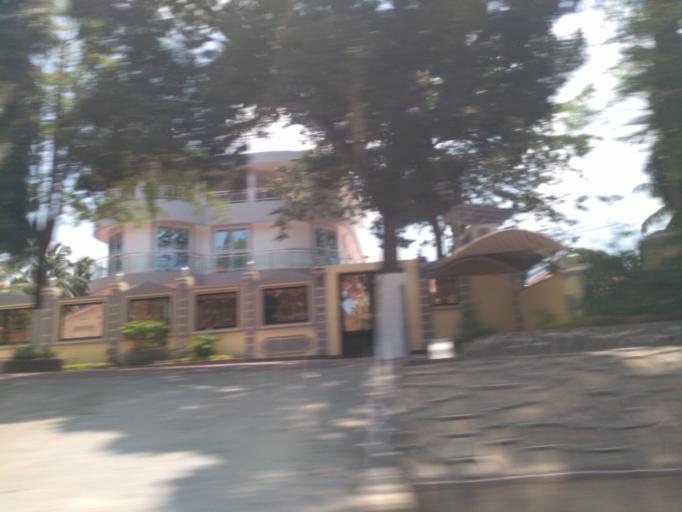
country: TZ
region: Dar es Salaam
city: Dar es Salaam
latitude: -6.8420
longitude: 39.3518
